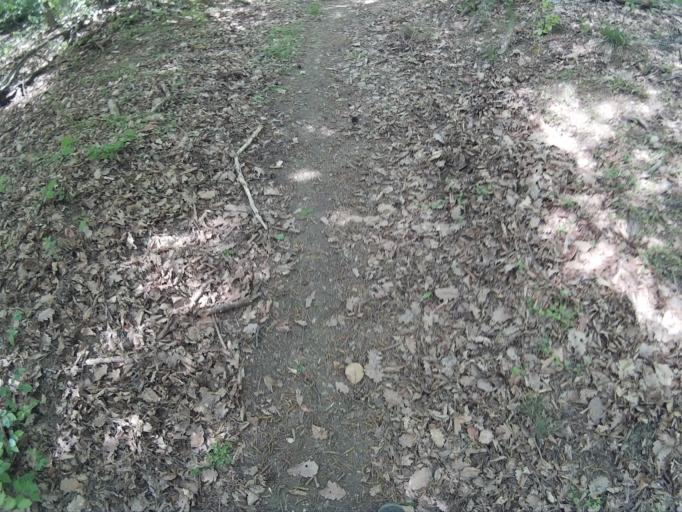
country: HU
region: Vas
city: Koszeg
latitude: 47.3567
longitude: 16.5049
